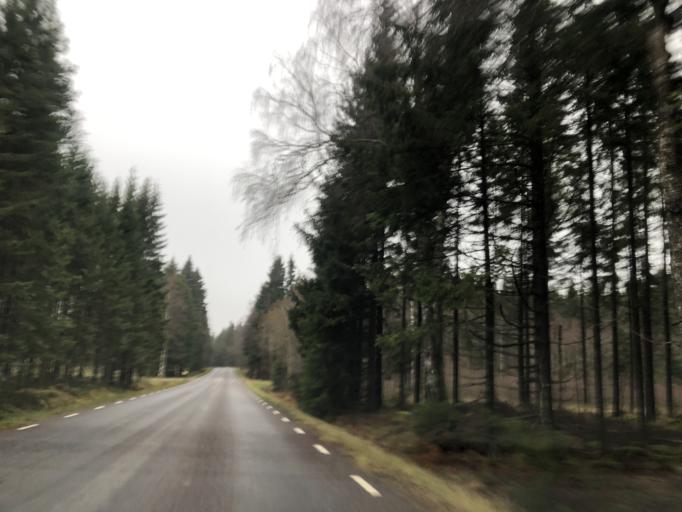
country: SE
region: Vaestra Goetaland
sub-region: Ulricehamns Kommun
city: Ulricehamn
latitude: 57.7600
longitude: 13.4897
